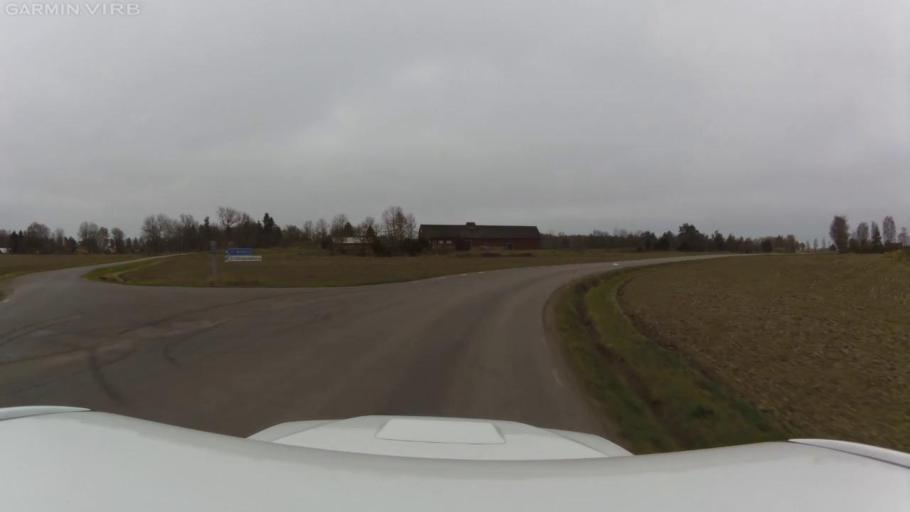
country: SE
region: OEstergoetland
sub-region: Linkopings Kommun
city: Vikingstad
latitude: 58.3671
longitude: 15.4315
